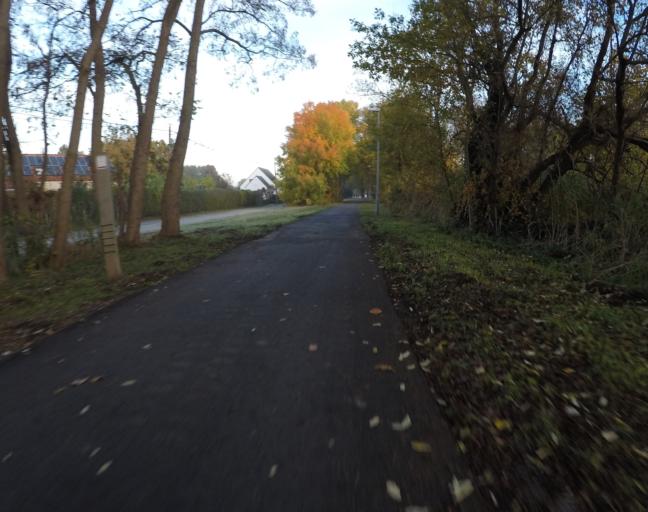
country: BE
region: Flanders
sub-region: Provincie Vlaams-Brabant
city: Begijnendijk
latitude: 51.0351
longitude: 4.8250
